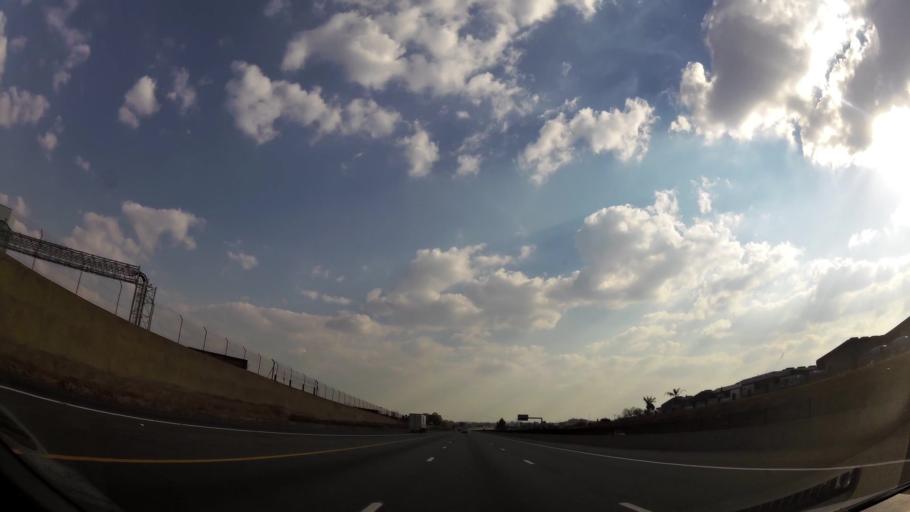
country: ZA
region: Gauteng
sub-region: Ekurhuleni Metropolitan Municipality
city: Germiston
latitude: -26.2563
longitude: 28.1856
